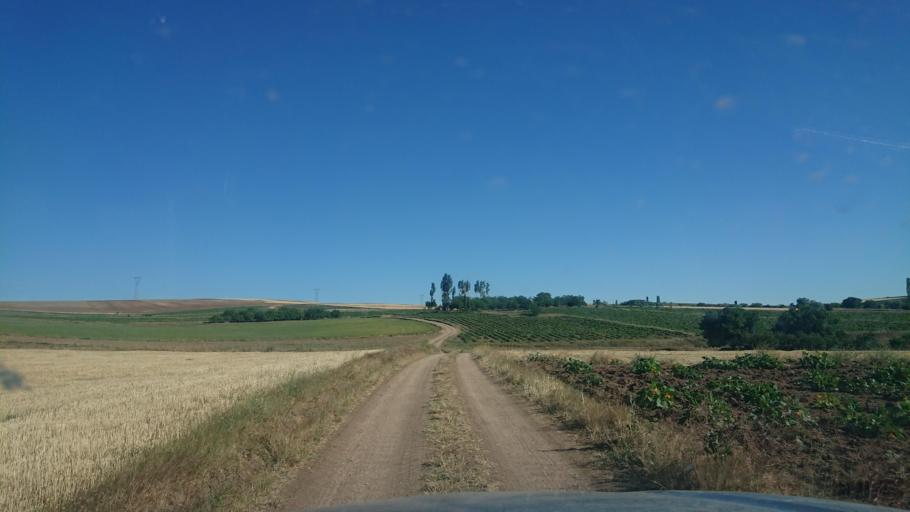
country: TR
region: Aksaray
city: Agacoren
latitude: 38.8294
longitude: 33.9529
